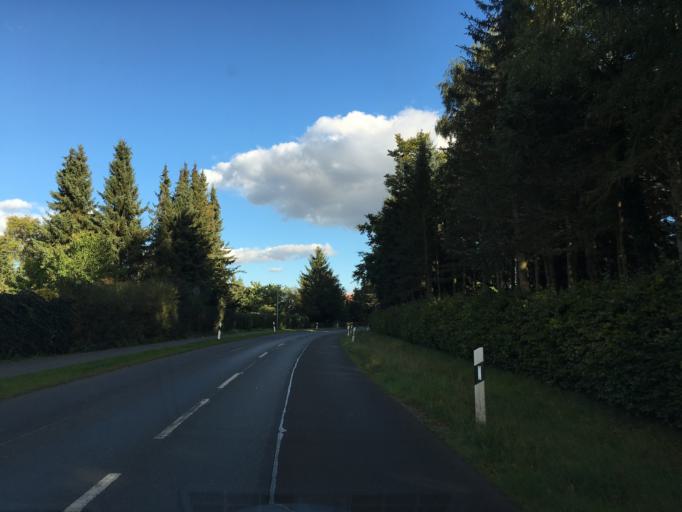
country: DE
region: Lower Saxony
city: Reppenstedt
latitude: 53.2478
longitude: 10.3646
